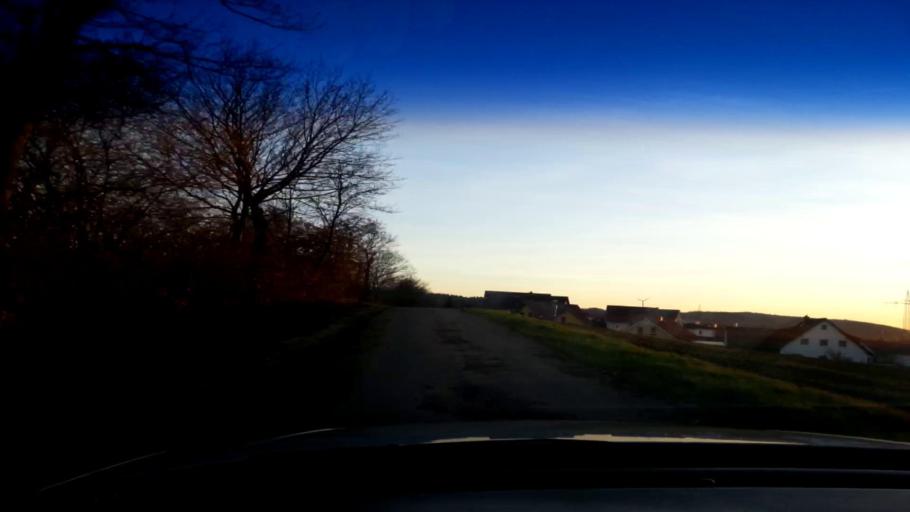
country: DE
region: Bavaria
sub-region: Upper Franconia
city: Zapfendorf
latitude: 50.0244
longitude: 10.9437
